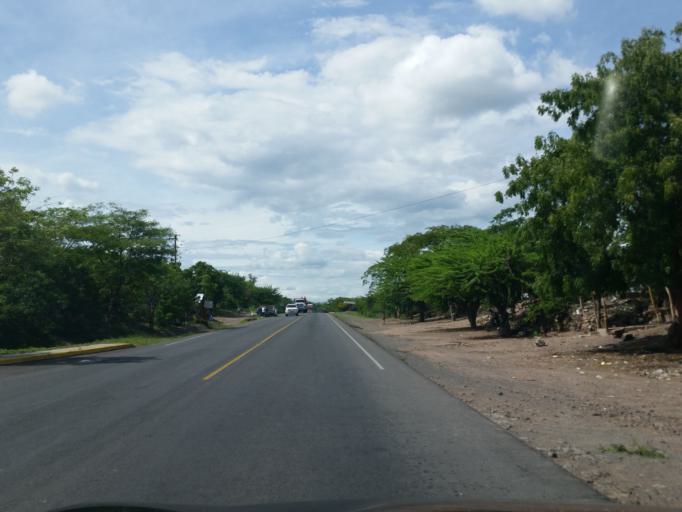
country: NI
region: Matagalpa
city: Ciudad Dario
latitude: 12.5384
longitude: -86.0492
